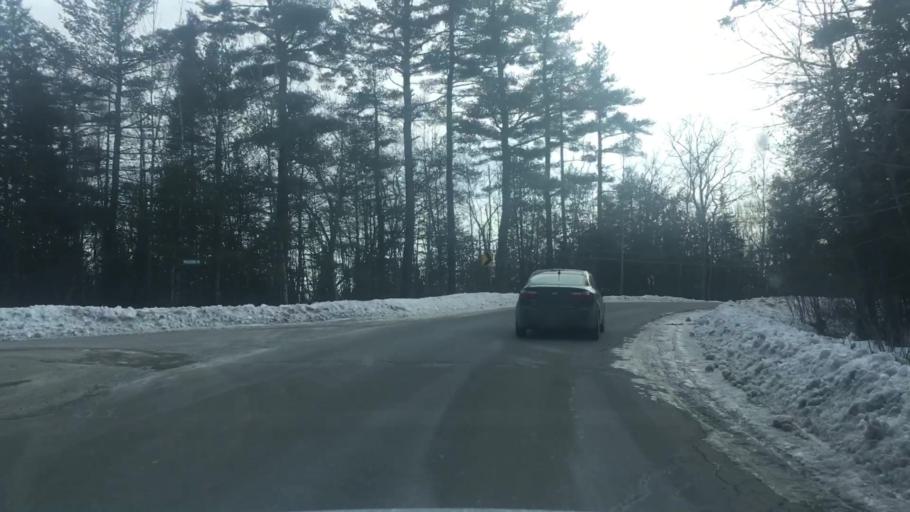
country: US
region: Maine
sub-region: Hancock County
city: Orland
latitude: 44.6278
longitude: -68.6985
